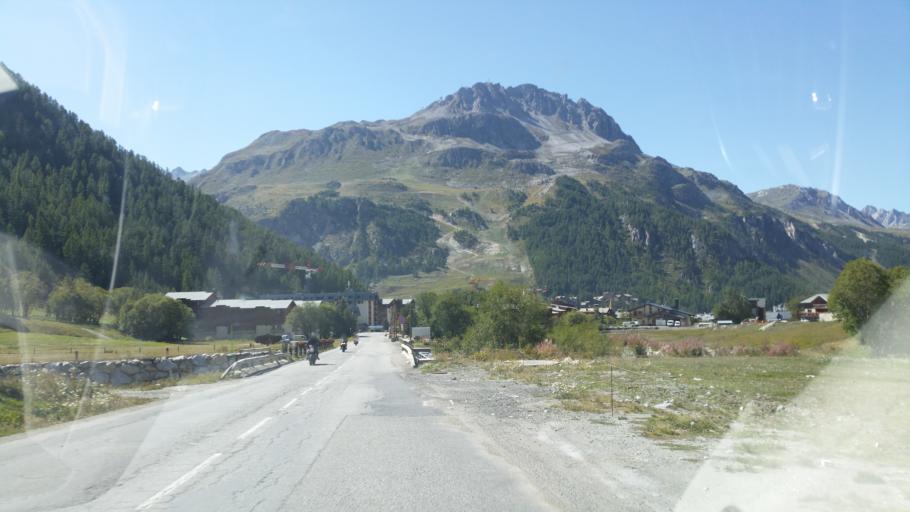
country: FR
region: Rhone-Alpes
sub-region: Departement de la Savoie
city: Val-d'Isere
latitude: 45.4473
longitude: 6.9920
